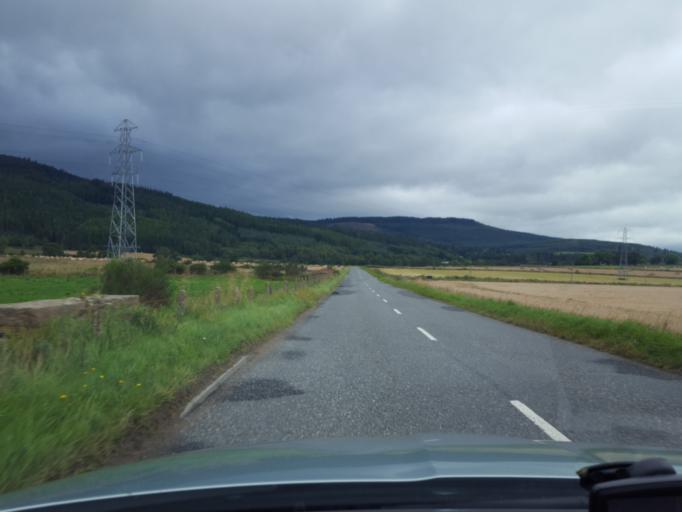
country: GB
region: Scotland
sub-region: Aberdeenshire
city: Banchory
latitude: 57.1394
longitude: -2.4534
